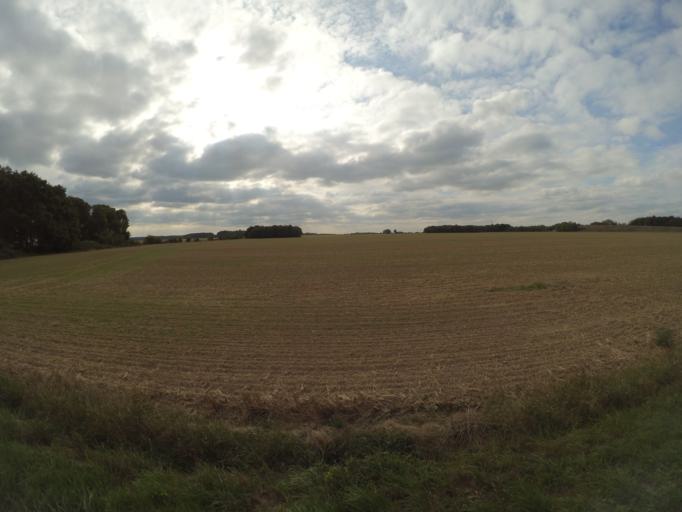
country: FR
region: Centre
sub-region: Departement d'Indre-et-Loire
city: Nazelles-Negron
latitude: 47.4834
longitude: 0.9385
